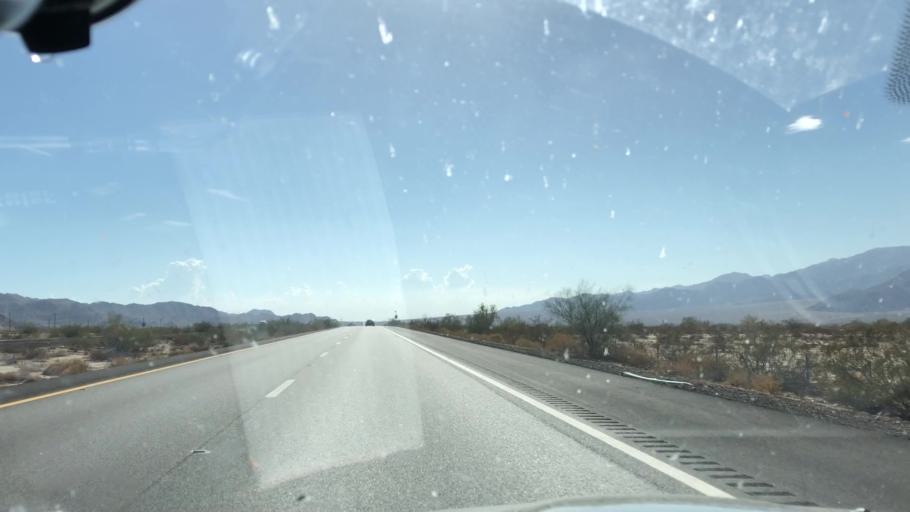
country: US
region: California
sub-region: Imperial County
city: Niland
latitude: 33.6723
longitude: -115.6021
